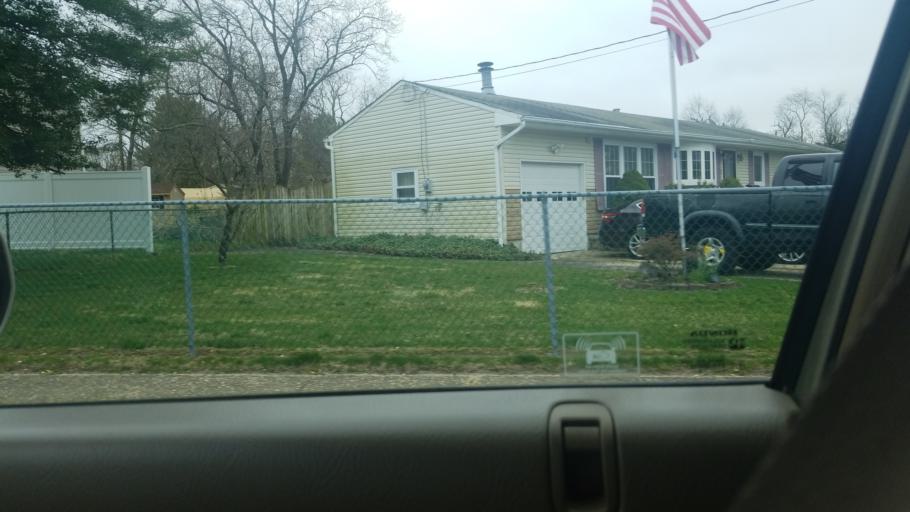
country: US
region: New Jersey
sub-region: Ocean County
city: Leisure Knoll
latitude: 40.0015
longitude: -74.2951
